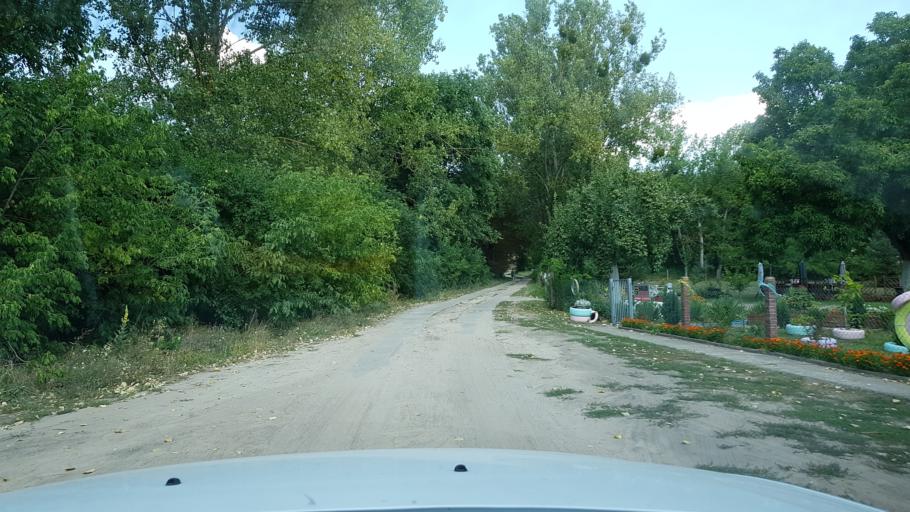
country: PL
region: West Pomeranian Voivodeship
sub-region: Powiat gryfinski
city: Cedynia
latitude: 52.8336
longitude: 14.1904
